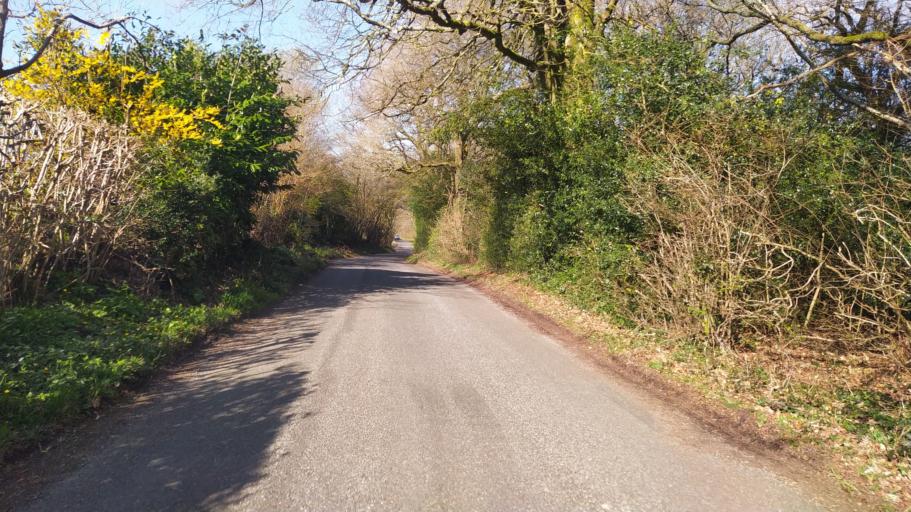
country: GB
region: England
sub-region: Dorset
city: Verwood
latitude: 50.8892
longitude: -1.9132
